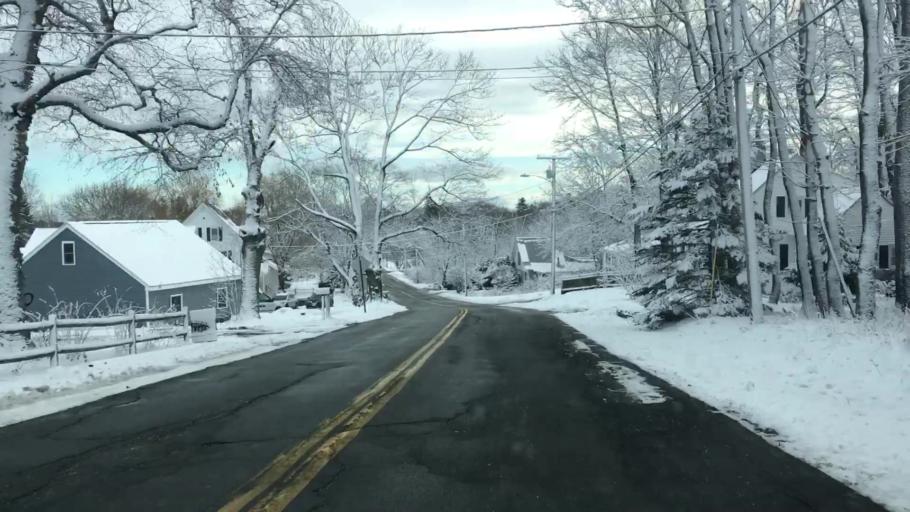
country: US
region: Maine
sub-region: Knox County
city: Rockland
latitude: 44.1103
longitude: -69.1255
